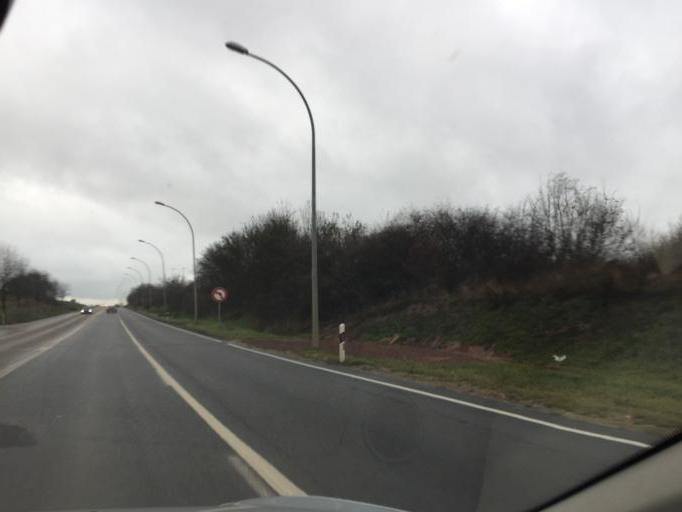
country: LU
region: Diekirch
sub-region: Canton de Diekirch
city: Diekirch
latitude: 49.8852
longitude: 6.1360
